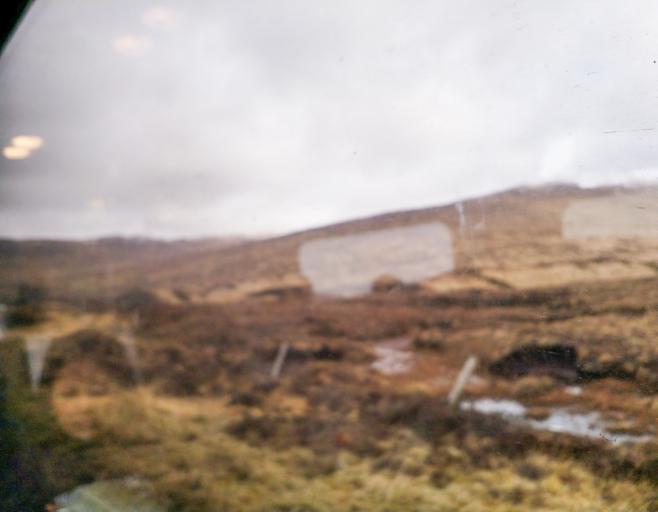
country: GB
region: Scotland
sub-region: Highland
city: Spean Bridge
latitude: 56.7642
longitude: -4.6975
